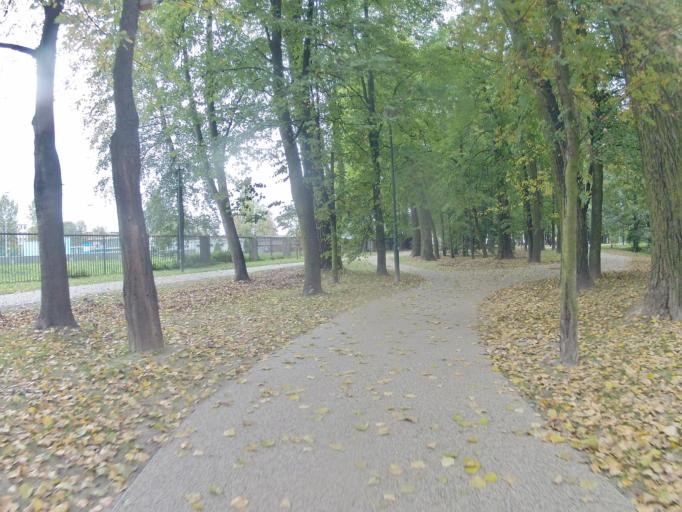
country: PL
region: Lesser Poland Voivodeship
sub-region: Krakow
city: Krakow
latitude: 50.0939
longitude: 19.9424
